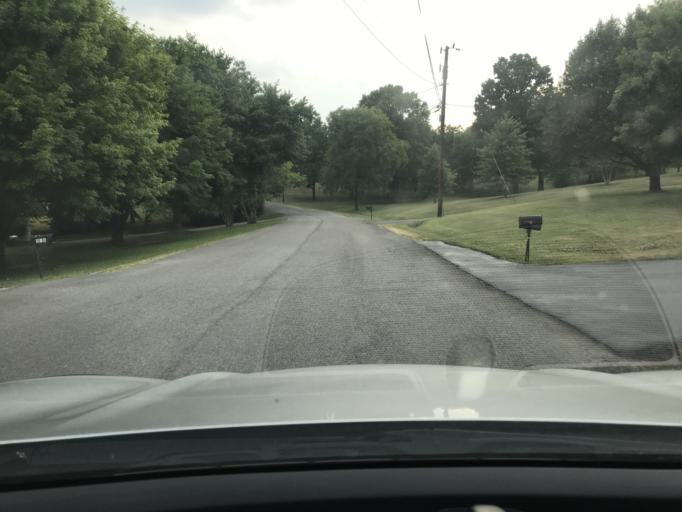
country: US
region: Tennessee
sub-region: Davidson County
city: Goodlettsville
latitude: 36.3018
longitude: -86.7128
